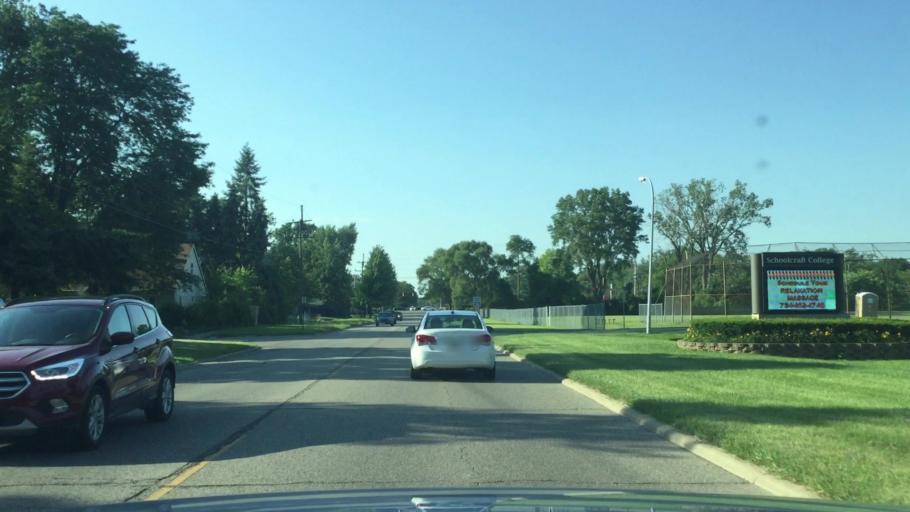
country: US
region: Michigan
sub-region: Wayne County
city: Westland
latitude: 42.3215
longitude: -83.3793
